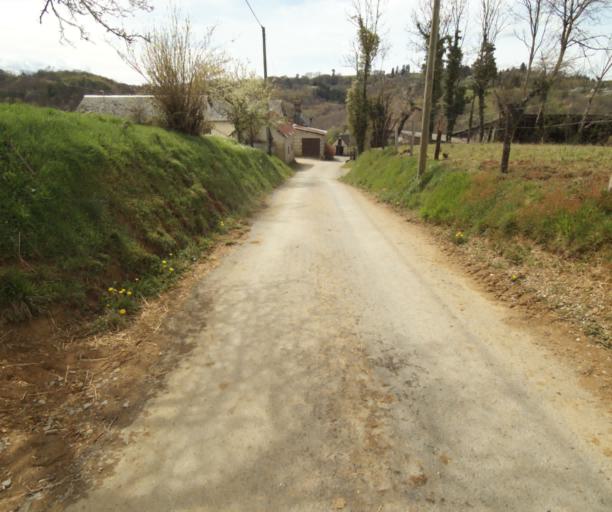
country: FR
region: Limousin
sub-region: Departement de la Correze
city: Laguenne
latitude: 45.2137
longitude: 1.8474
